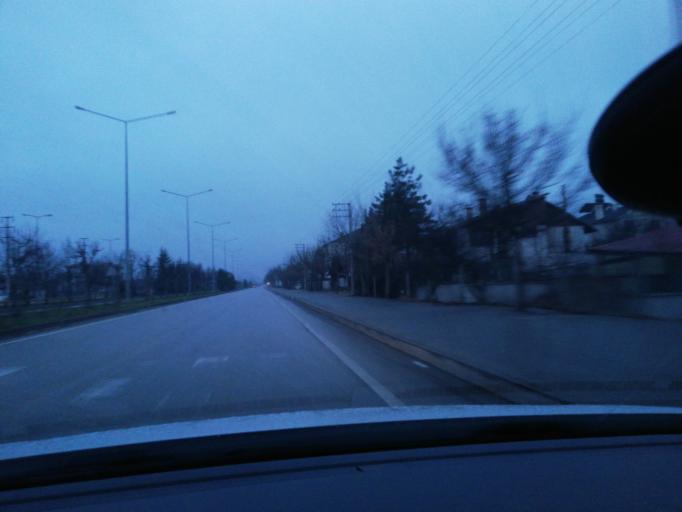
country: TR
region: Bolu
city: Bolu
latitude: 40.7225
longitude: 31.6128
